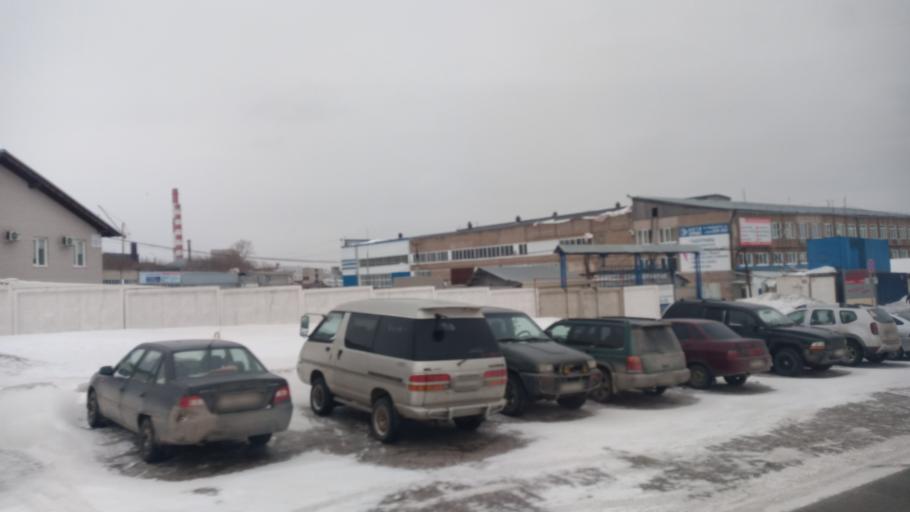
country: RU
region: Altai Krai
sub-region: Gorod Barnaulskiy
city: Barnaul
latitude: 53.3881
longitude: 83.6797
